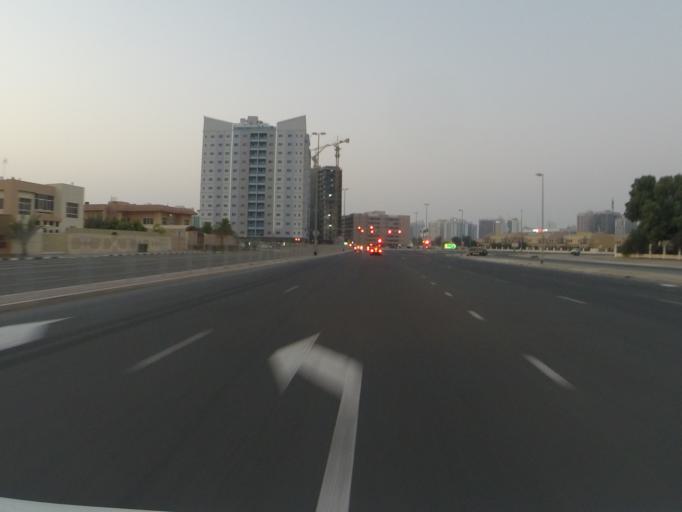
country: AE
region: Dubai
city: Dubai
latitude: 25.1044
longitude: 55.1994
